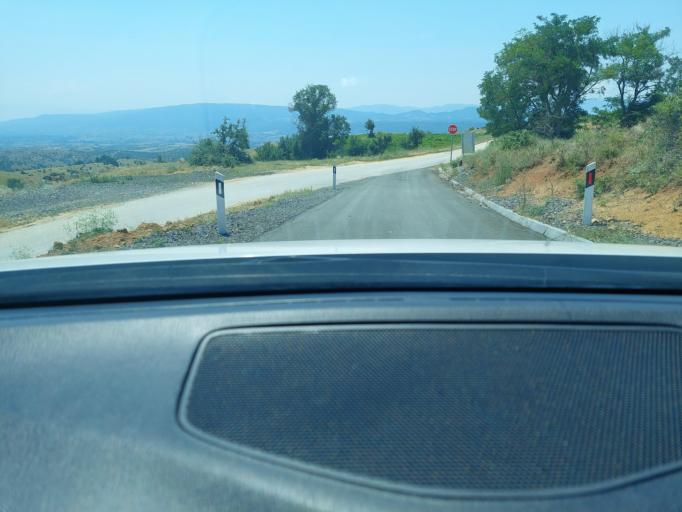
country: MK
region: Radovis
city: Radovish
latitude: 41.6589
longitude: 22.4102
